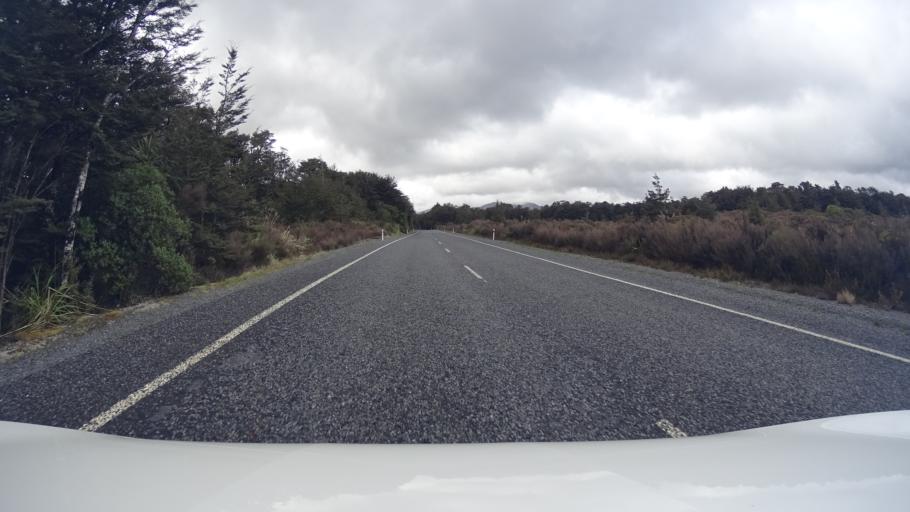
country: NZ
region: Manawatu-Wanganui
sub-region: Ruapehu District
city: Waiouru
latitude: -39.1765
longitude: 175.5150
